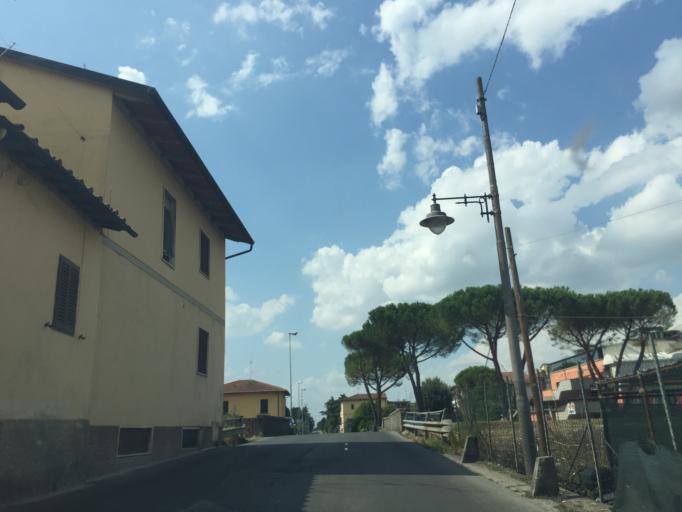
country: IT
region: Tuscany
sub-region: Province of Florence
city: San Donnino
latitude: 43.7964
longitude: 11.1487
